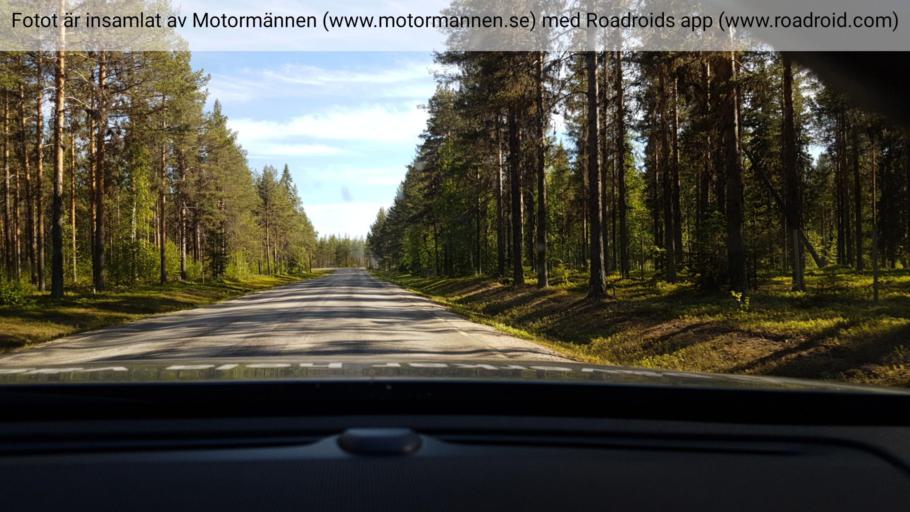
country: SE
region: Vaesterbotten
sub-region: Norsjo Kommun
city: Norsjoe
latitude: 64.7239
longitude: 19.1325
